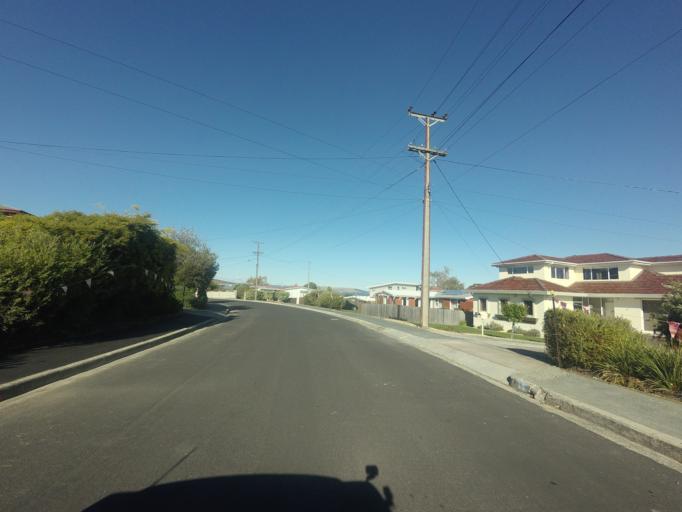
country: AU
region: Tasmania
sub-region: Clarence
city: Bellerive
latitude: -42.8733
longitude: 147.3544
